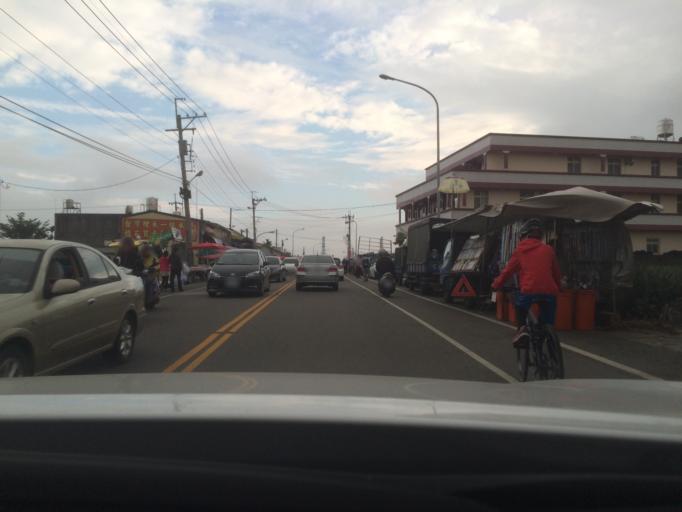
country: TW
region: Taiwan
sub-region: Nantou
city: Nantou
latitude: 23.9330
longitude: 120.6380
